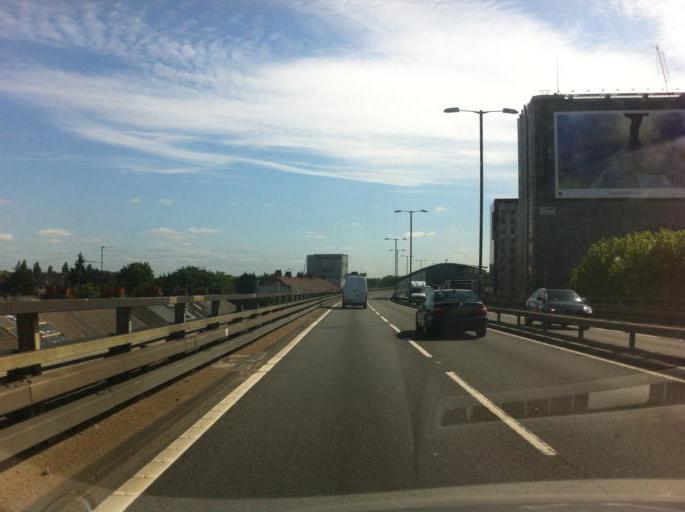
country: GB
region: England
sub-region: Greater London
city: Brentford
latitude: 51.4903
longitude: -0.3079
